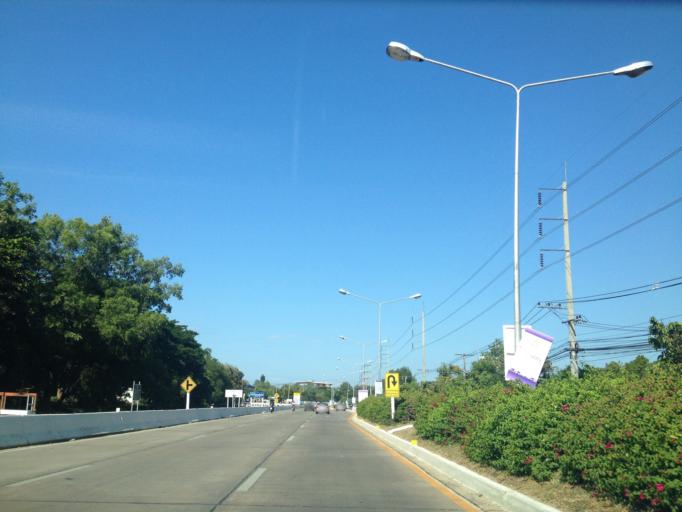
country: TH
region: Chiang Mai
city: Chiang Mai
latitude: 18.8146
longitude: 98.9633
